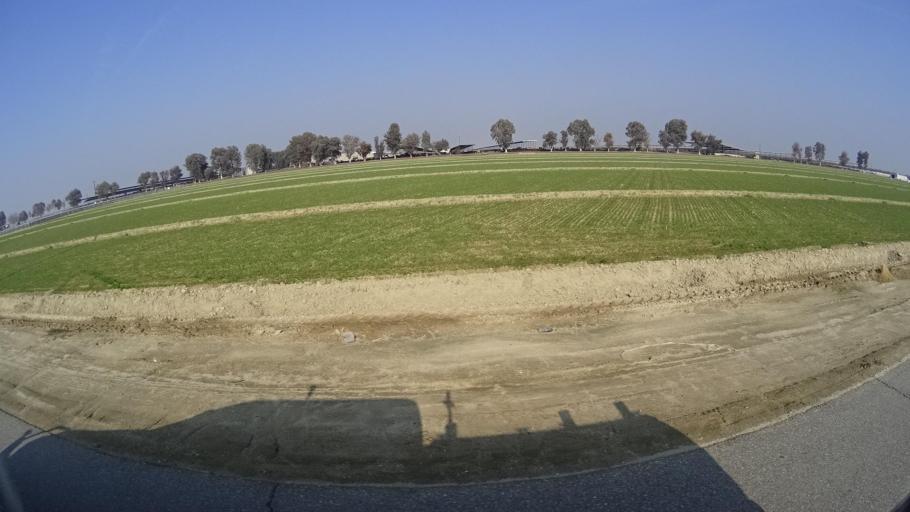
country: US
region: California
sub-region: Kern County
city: Shafter
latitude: 35.3546
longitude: -119.3192
